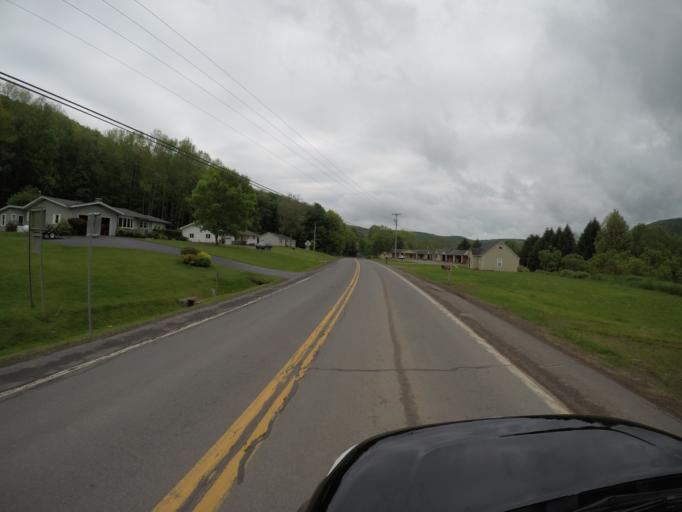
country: US
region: New York
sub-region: Delaware County
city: Delhi
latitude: 42.2655
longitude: -74.9181
